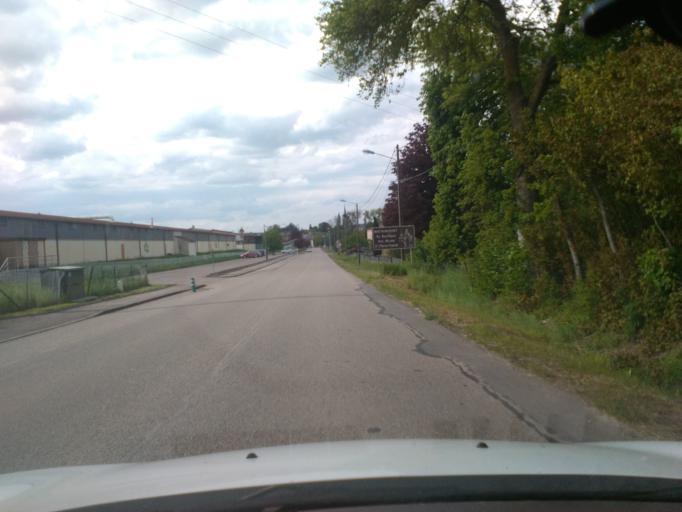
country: FR
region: Lorraine
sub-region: Departement des Vosges
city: Mirecourt
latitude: 48.2729
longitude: 6.1374
